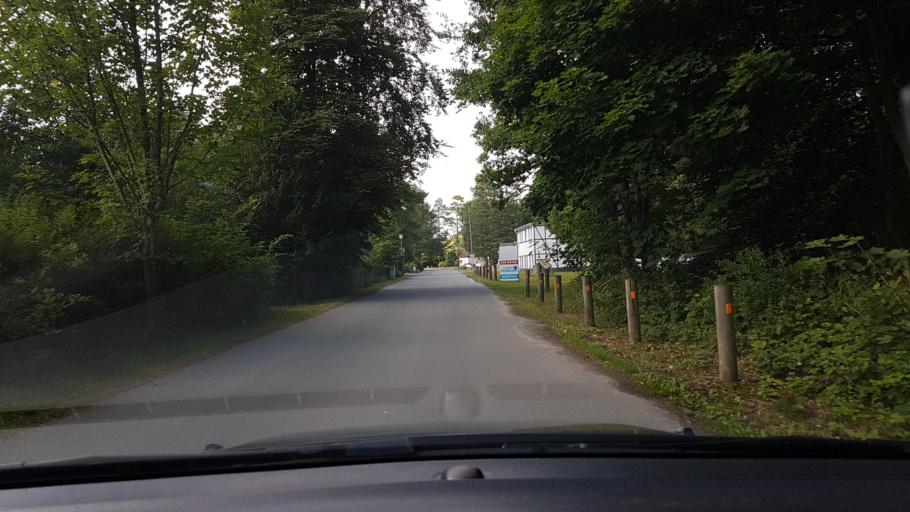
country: DE
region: Lower Saxony
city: Fassberg
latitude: 52.8732
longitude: 10.2265
